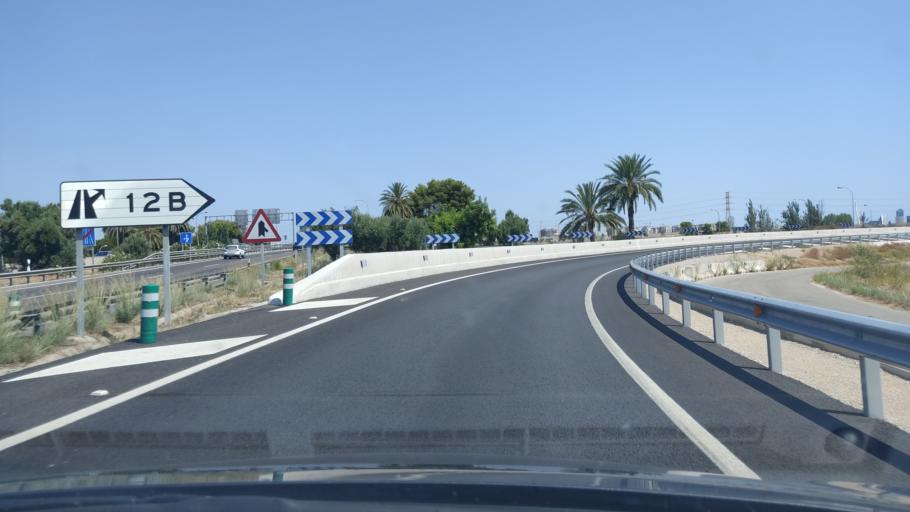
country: ES
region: Valencia
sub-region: Provincia de Valencia
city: Sedavi
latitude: 39.4328
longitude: -0.3703
